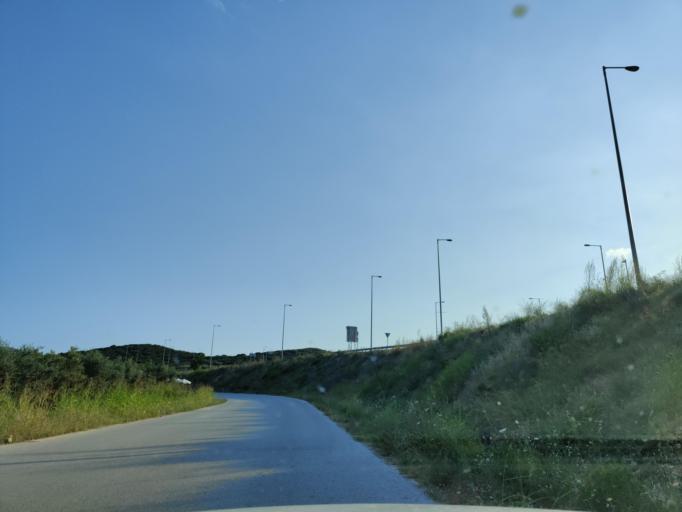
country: GR
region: East Macedonia and Thrace
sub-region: Nomos Kavalas
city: Nea Peramos
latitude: 40.8227
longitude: 24.2859
